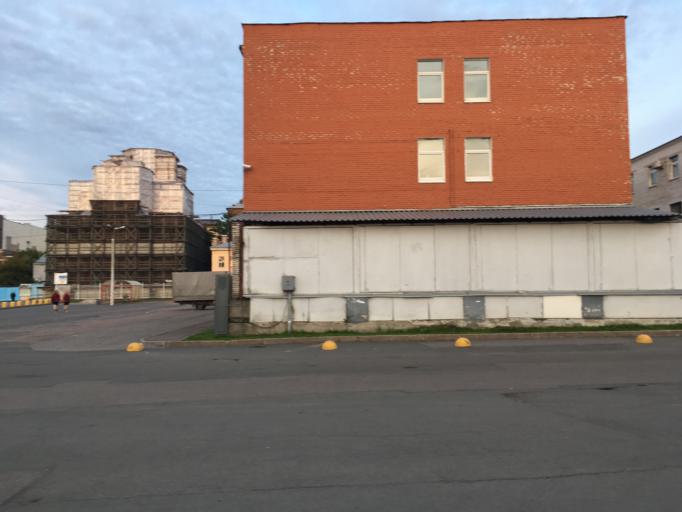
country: RU
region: St.-Petersburg
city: Centralniy
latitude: 59.9147
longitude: 30.3421
